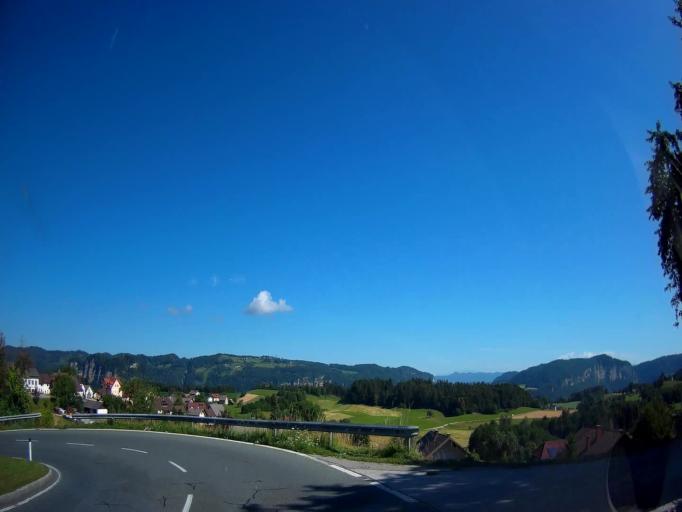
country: AT
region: Carinthia
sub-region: Politischer Bezirk Klagenfurt Land
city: Grafenstein
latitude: 46.5404
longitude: 14.4238
